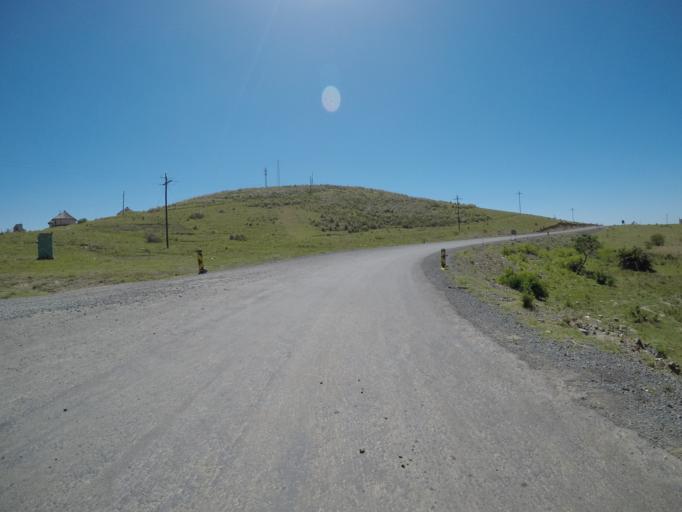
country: ZA
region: Eastern Cape
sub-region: OR Tambo District Municipality
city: Libode
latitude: -32.0006
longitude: 29.1172
